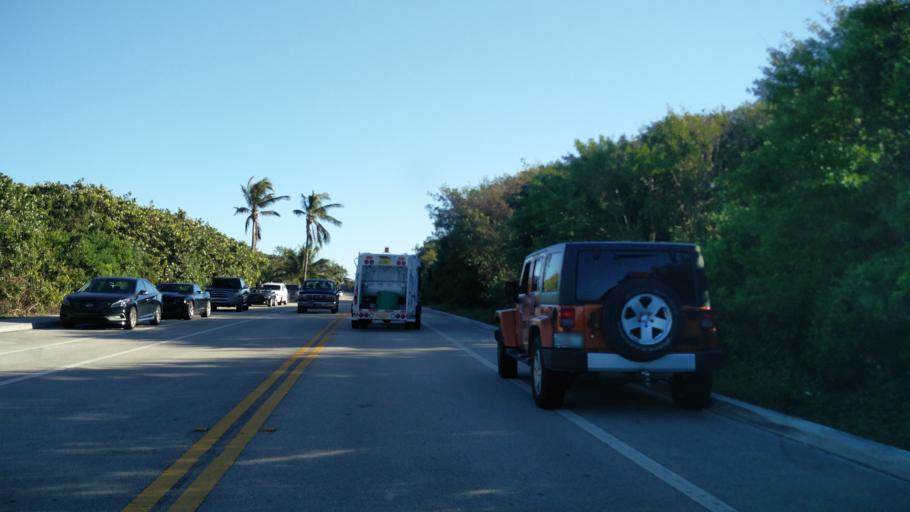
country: US
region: Florida
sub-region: Palm Beach County
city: Juno Beach
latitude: 26.9129
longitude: -80.0637
